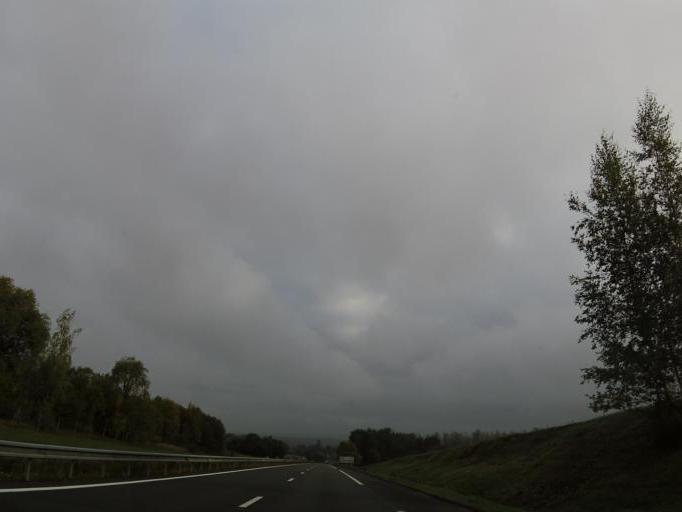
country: FR
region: Ile-de-France
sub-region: Departement de Seine-et-Marne
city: Saint-Jean-les-Deux-Jumeaux
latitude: 48.9355
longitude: 3.0281
